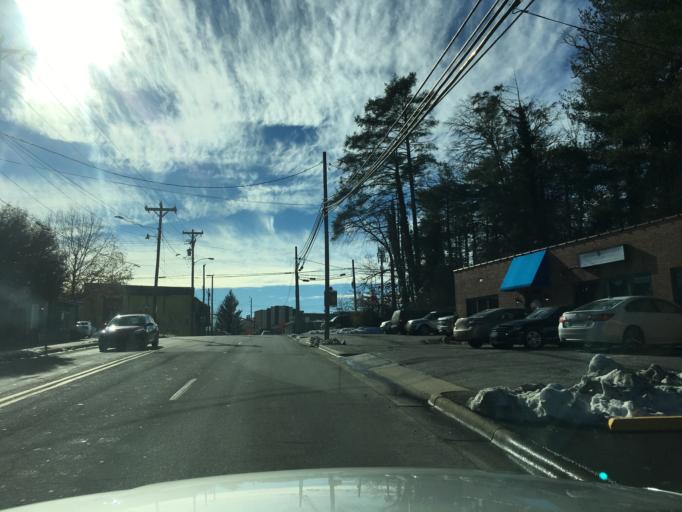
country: US
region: North Carolina
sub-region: Transylvania County
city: Brevard
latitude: 35.2356
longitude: -82.7343
